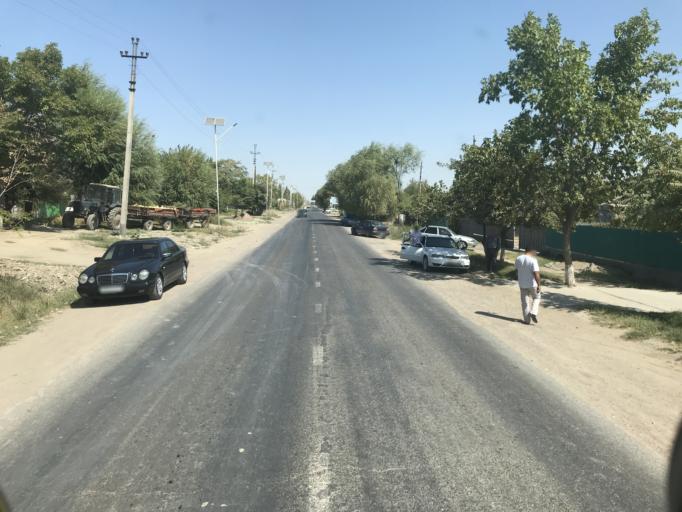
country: KZ
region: Ongtustik Qazaqstan
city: Ilyich
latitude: 40.9332
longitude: 68.4883
